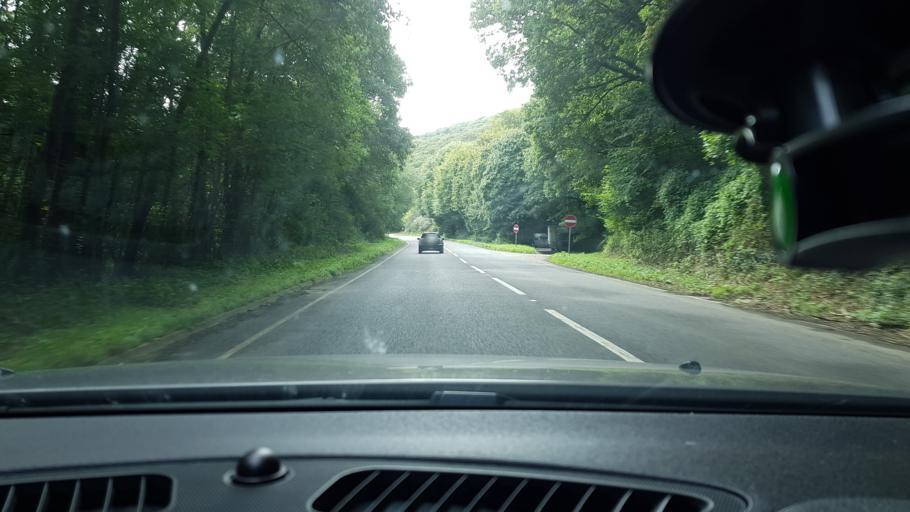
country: GB
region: England
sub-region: Cornwall
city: Helland
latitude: 50.5693
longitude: -4.7477
